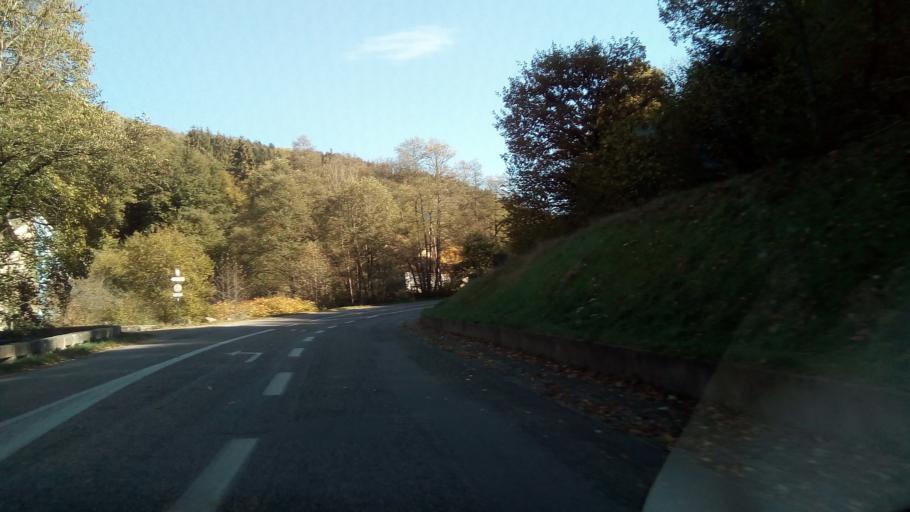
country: FR
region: Alsace
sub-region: Departement du Bas-Rhin
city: Rothau
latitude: 48.4171
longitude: 7.1961
